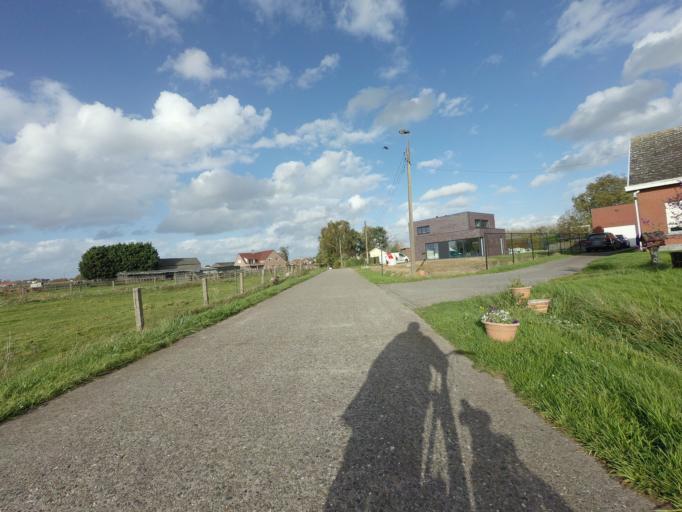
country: BE
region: Flanders
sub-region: Provincie Vlaams-Brabant
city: Zemst
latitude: 51.0065
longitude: 4.4382
